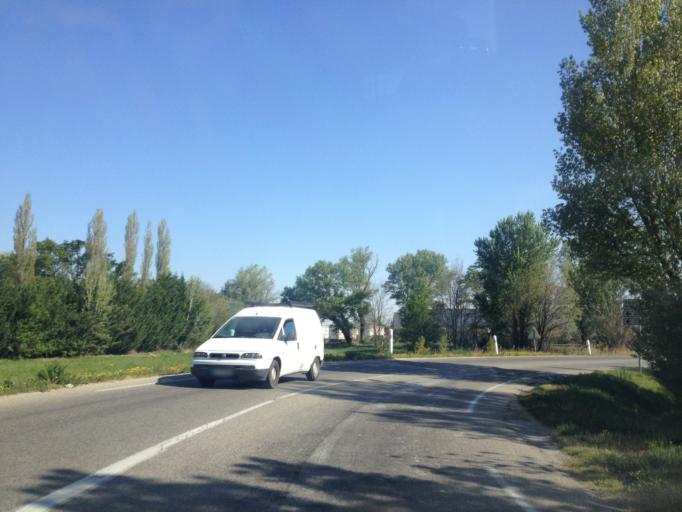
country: FR
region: Provence-Alpes-Cote d'Azur
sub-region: Departement du Vaucluse
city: Jonquieres
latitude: 44.1070
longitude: 4.9156
